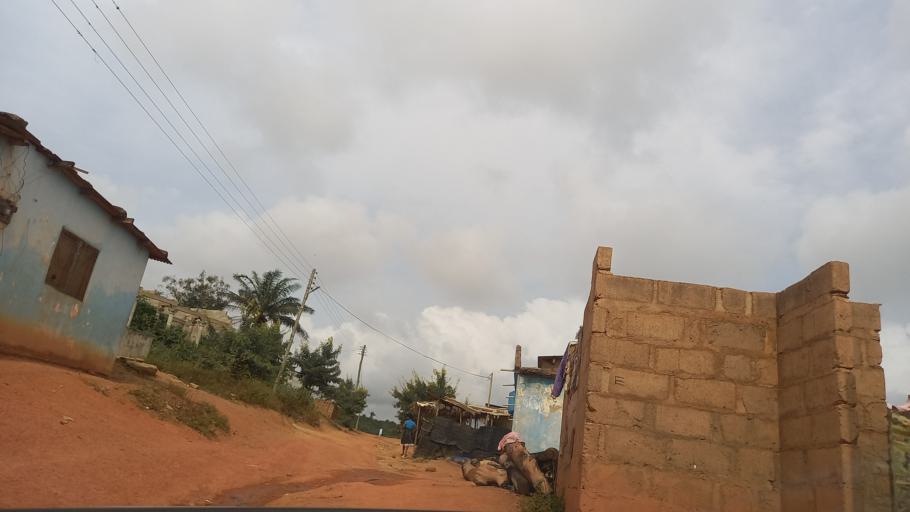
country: GH
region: Western
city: Shama Junction
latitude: 4.9862
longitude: -1.6388
